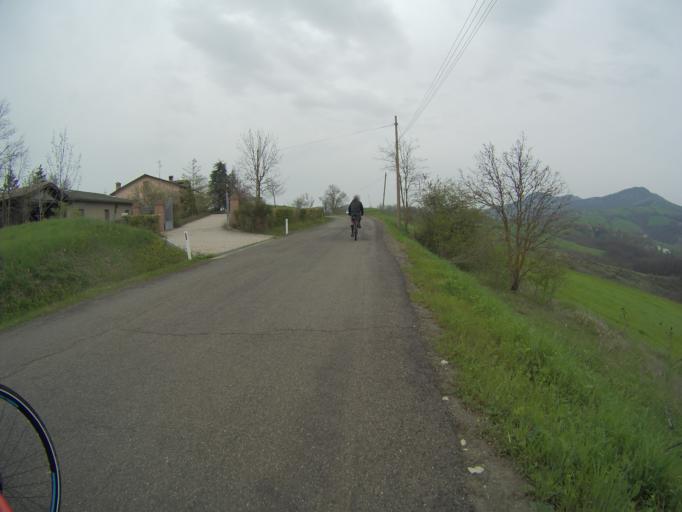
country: IT
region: Emilia-Romagna
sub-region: Provincia di Reggio Emilia
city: Ciano d'Enza
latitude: 44.5412
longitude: 10.4246
